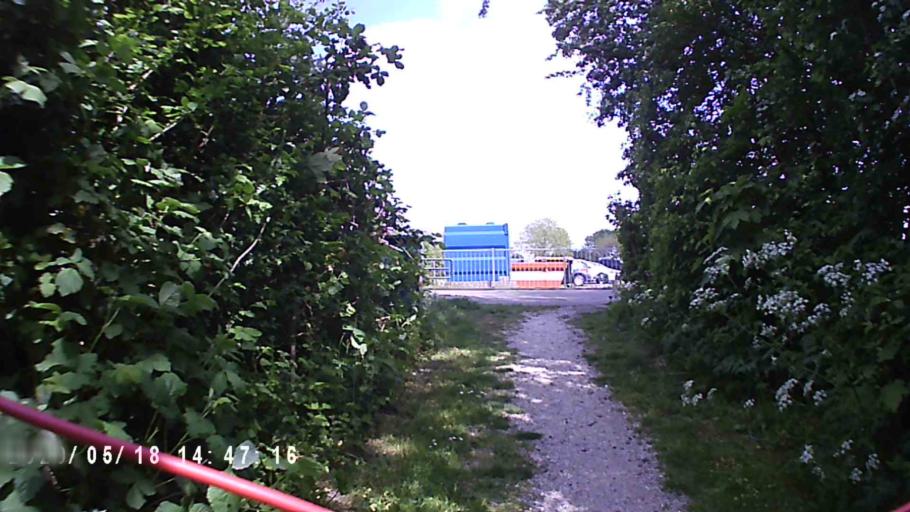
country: NL
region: Groningen
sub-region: Gemeente Winsum
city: Winsum
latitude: 53.3343
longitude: 6.5095
